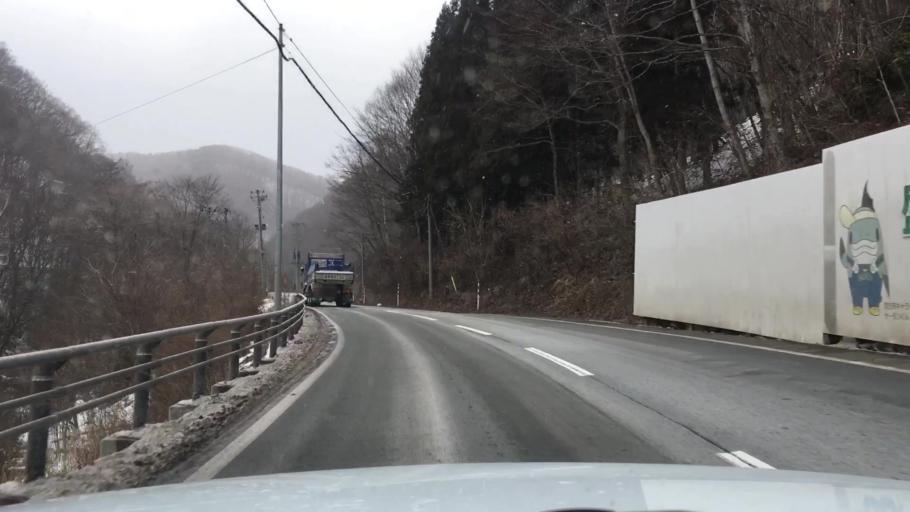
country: JP
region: Iwate
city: Tono
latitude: 39.6262
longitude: 141.4681
